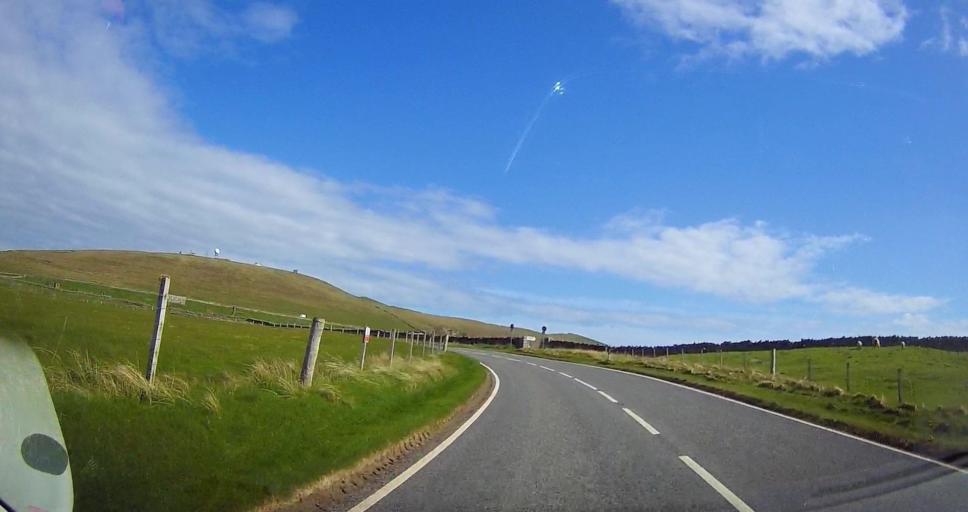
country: GB
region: Scotland
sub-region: Shetland Islands
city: Sandwick
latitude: 59.8713
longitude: -1.2867
